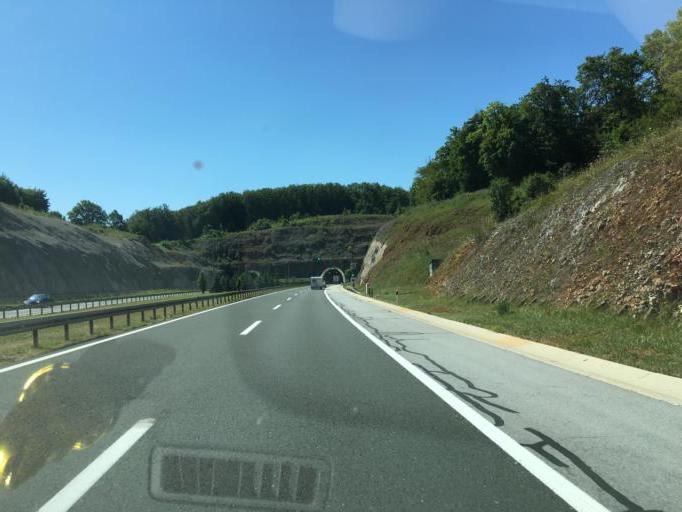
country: HR
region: Licko-Senjska
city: Otocac
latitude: 44.8764
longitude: 15.2056
